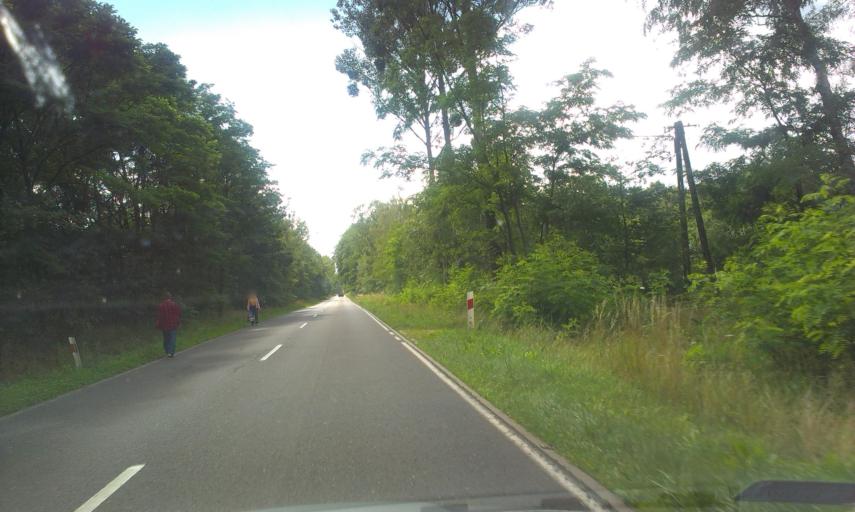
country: PL
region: Lodz Voivodeship
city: Zabia Wola
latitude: 51.9662
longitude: 20.6856
